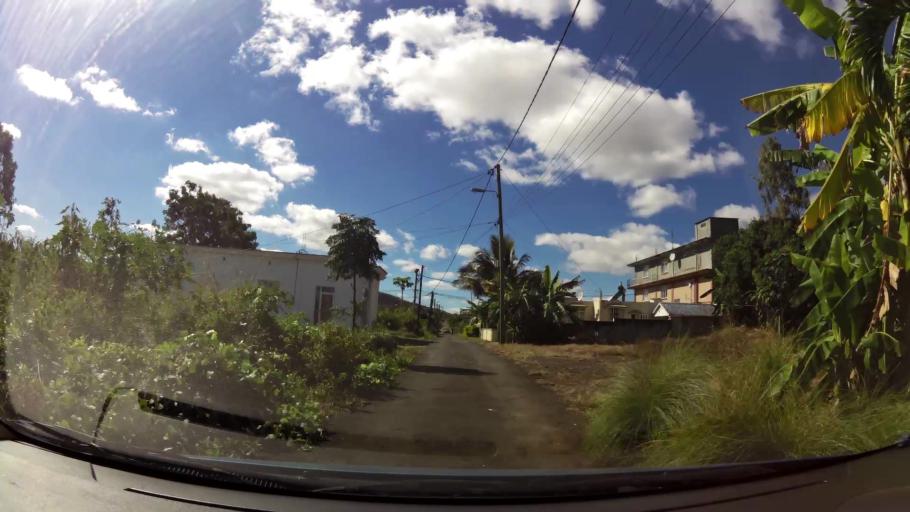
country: MU
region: Plaines Wilhems
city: Vacoas
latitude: -20.2894
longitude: 57.4749
